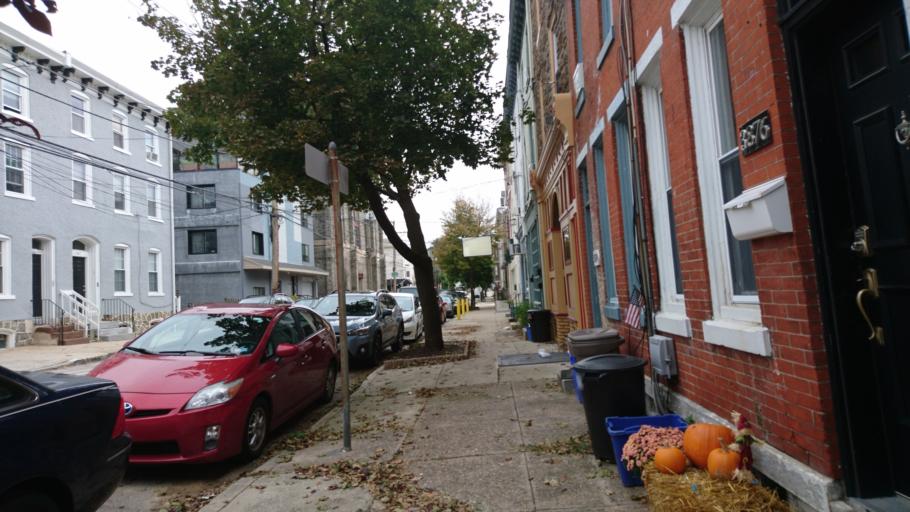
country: US
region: Pennsylvania
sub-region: Montgomery County
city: Bala-Cynwyd
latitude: 40.0211
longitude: -75.2131
